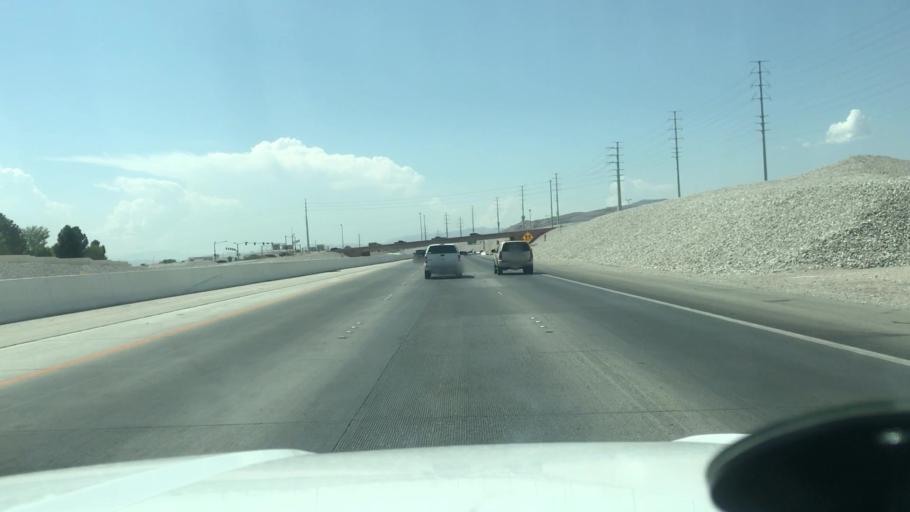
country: US
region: Nevada
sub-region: Clark County
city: Summerlin South
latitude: 36.1954
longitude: -115.3422
